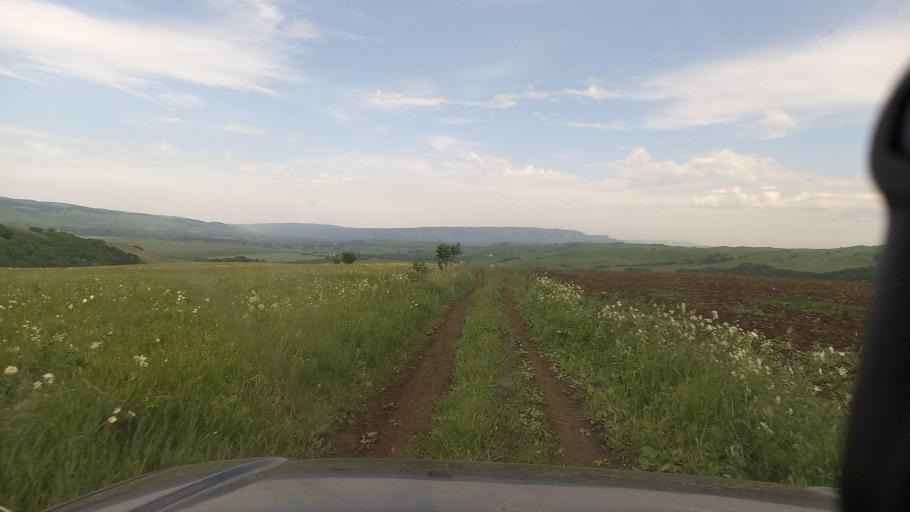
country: RU
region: Krasnodarskiy
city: Peredovaya
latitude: 44.0783
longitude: 41.3323
